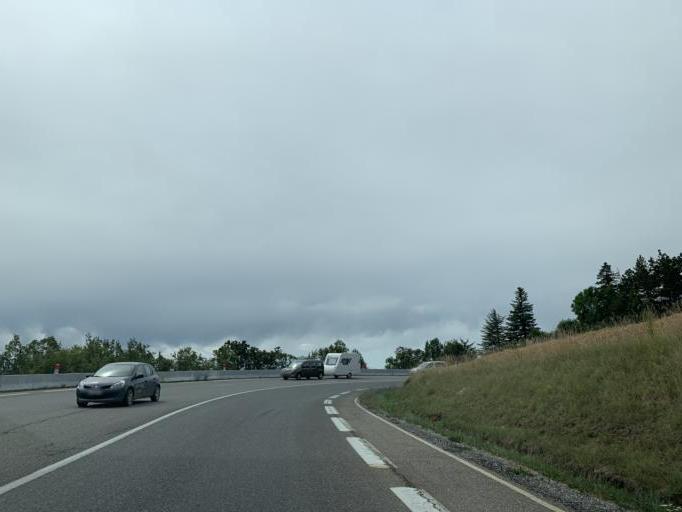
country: FR
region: Provence-Alpes-Cote d'Azur
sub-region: Departement des Hautes-Alpes
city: Gap
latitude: 44.5487
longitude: 6.0381
